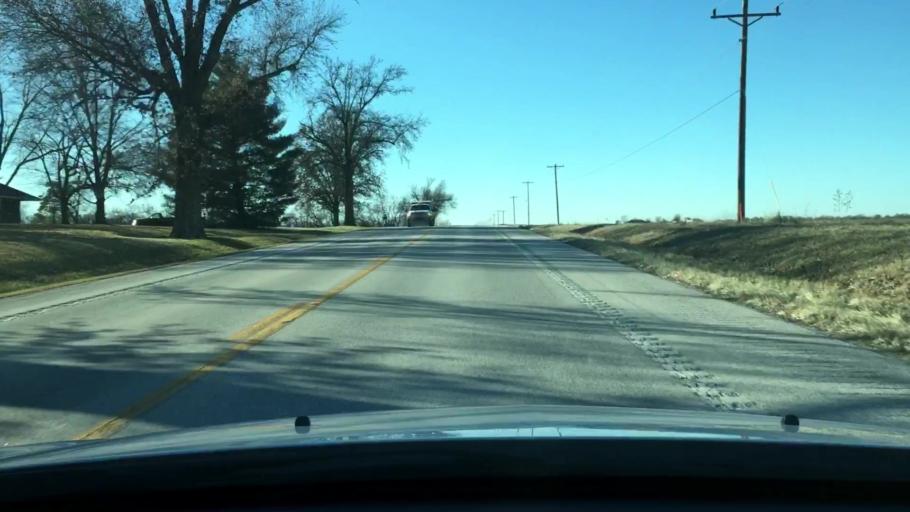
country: US
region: Missouri
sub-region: Pike County
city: Bowling Green
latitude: 39.3445
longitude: -91.2800
